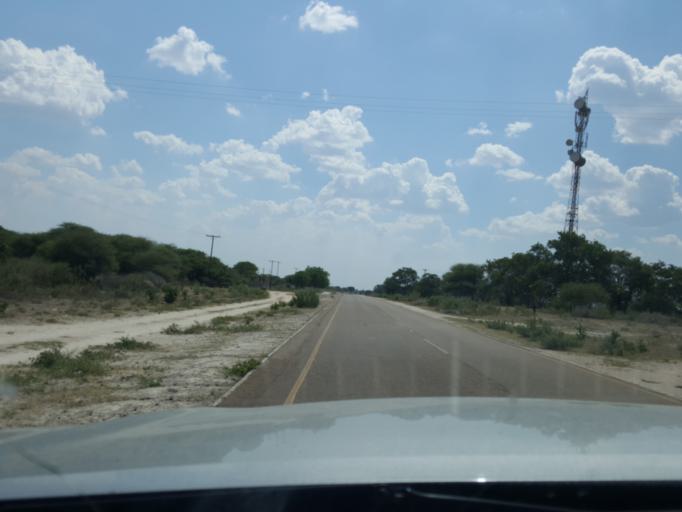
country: BW
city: Nokaneng
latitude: -19.6624
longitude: 22.1878
